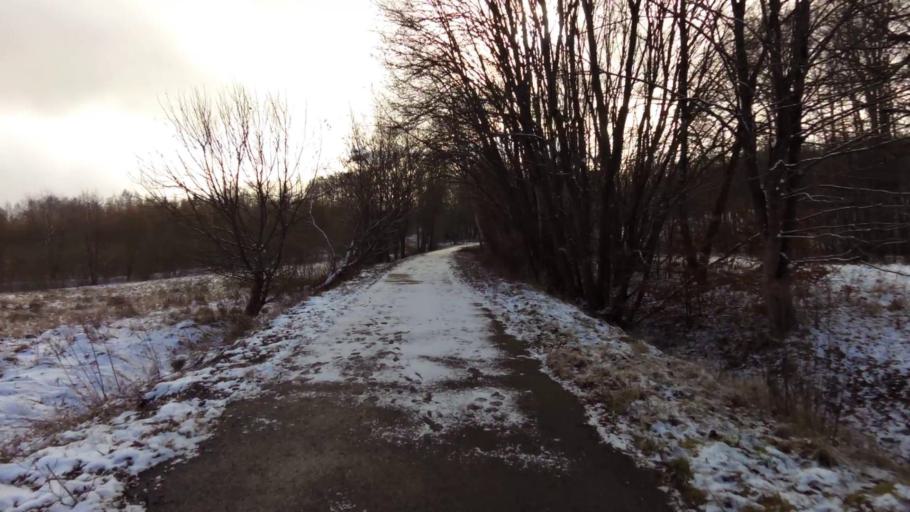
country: PL
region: West Pomeranian Voivodeship
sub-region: Powiat swidwinski
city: Polczyn-Zdroj
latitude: 53.7481
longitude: 16.0622
